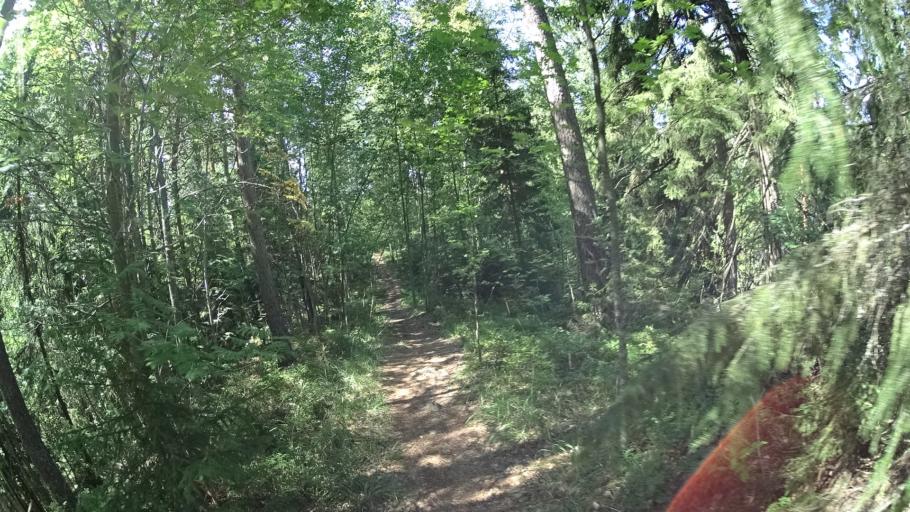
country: FI
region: Haeme
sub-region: Forssa
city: Tammela
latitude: 60.7732
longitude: 23.8471
